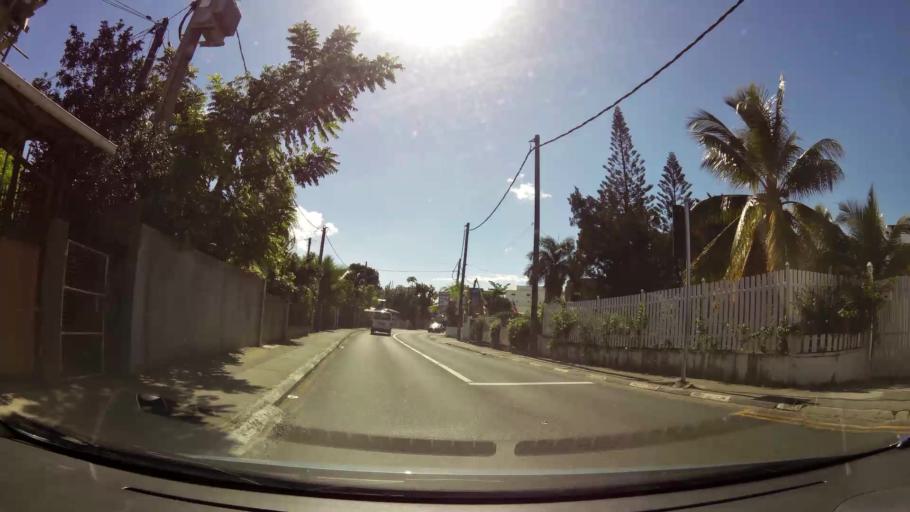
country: MU
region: Black River
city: Flic en Flac
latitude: -20.2787
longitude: 57.3687
